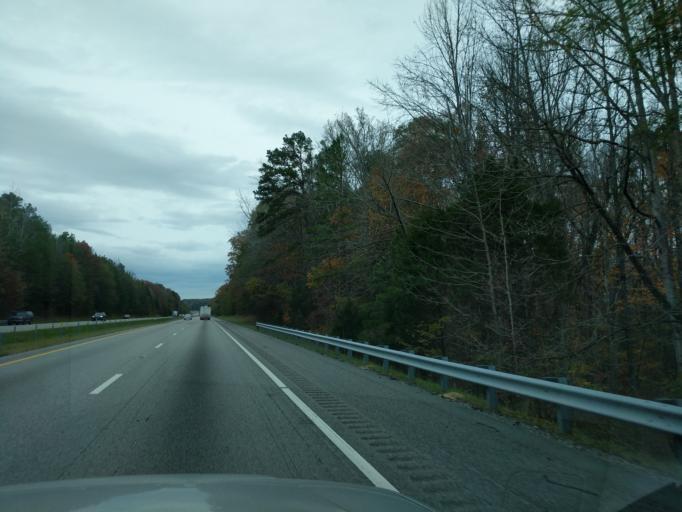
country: US
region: South Carolina
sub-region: Laurens County
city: Clinton
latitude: 34.5869
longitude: -81.8925
